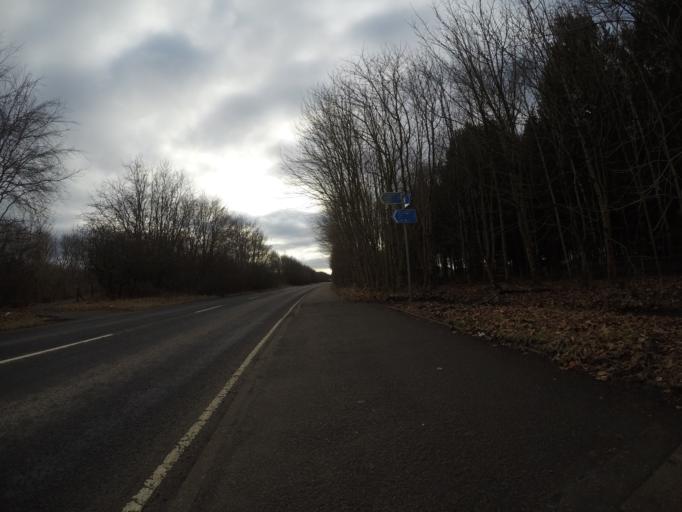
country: GB
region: Scotland
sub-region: North Ayrshire
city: Irvine
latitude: 55.5912
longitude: -4.6514
